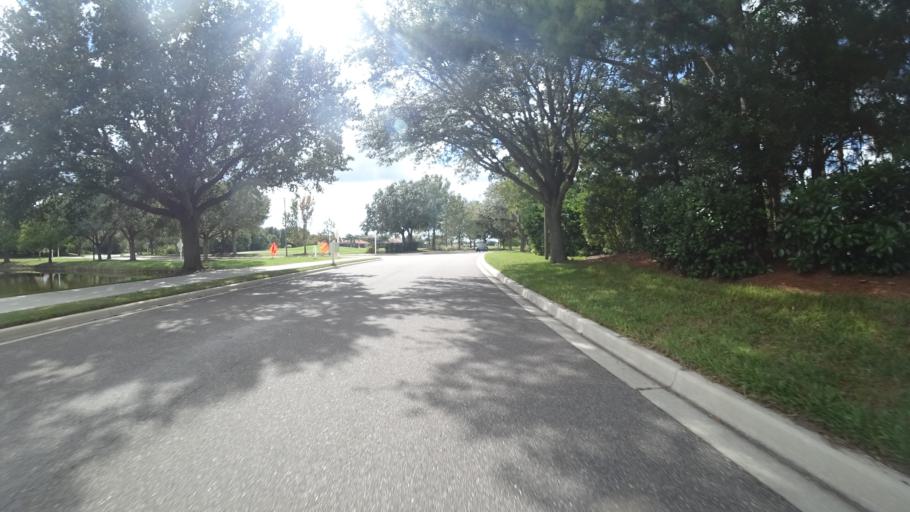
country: US
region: Florida
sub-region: Sarasota County
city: The Meadows
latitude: 27.3951
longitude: -82.4014
